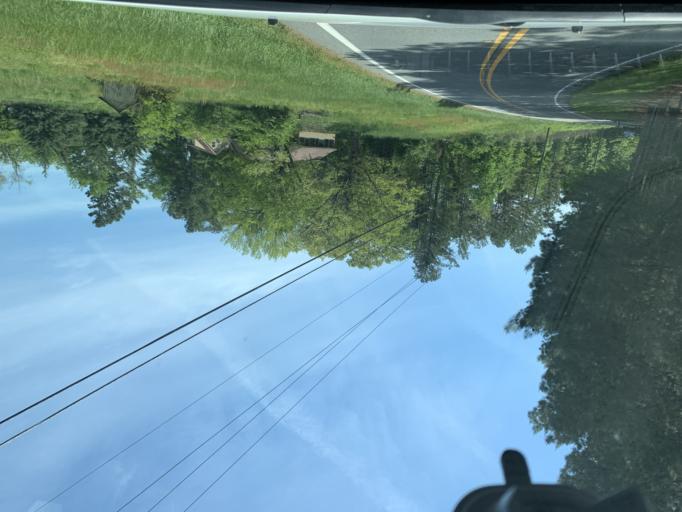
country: US
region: Georgia
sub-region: Forsyth County
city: Cumming
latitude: 34.2731
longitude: -84.2021
